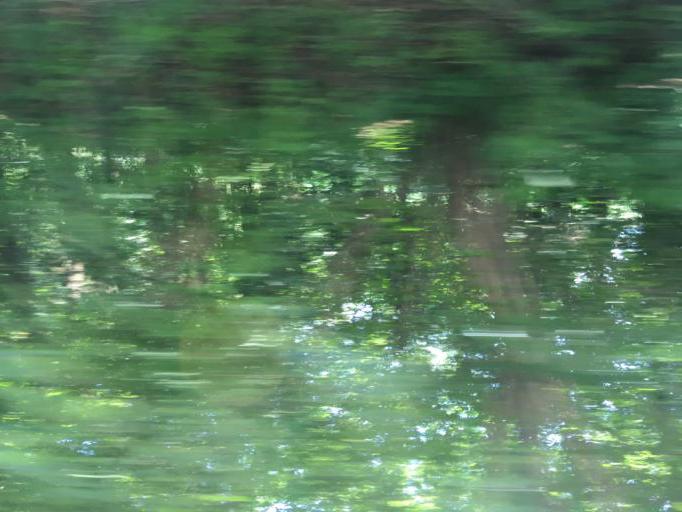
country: SI
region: Metlika
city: Metlika
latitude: 45.5885
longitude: 15.3443
